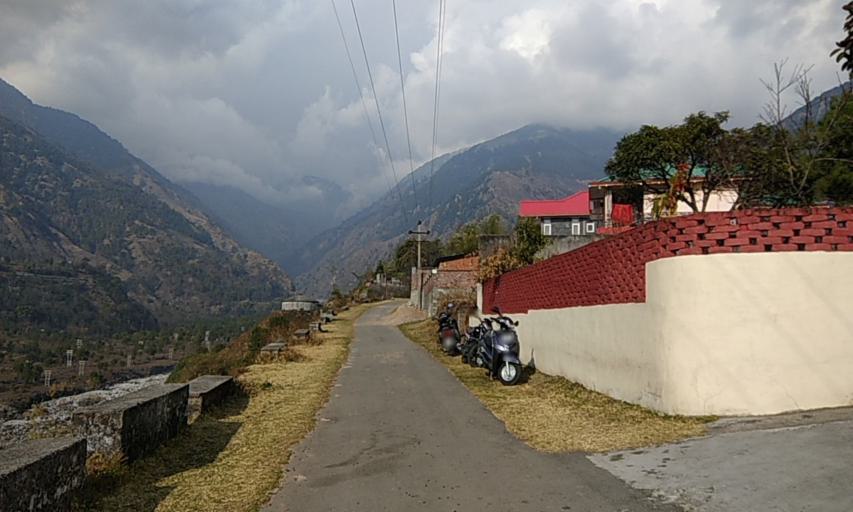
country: IN
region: Himachal Pradesh
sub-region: Kangra
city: Palampur
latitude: 32.1385
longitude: 76.5369
